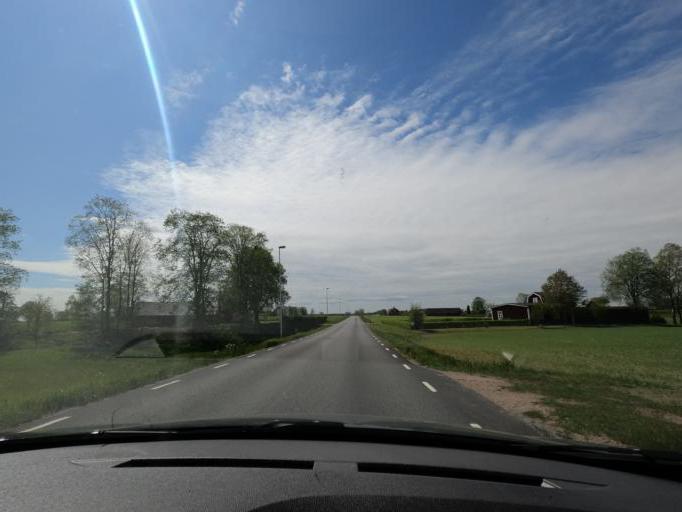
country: SE
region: Joenkoeping
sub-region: Varnamo Kommun
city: Bredaryd
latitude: 57.1337
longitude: 13.7078
